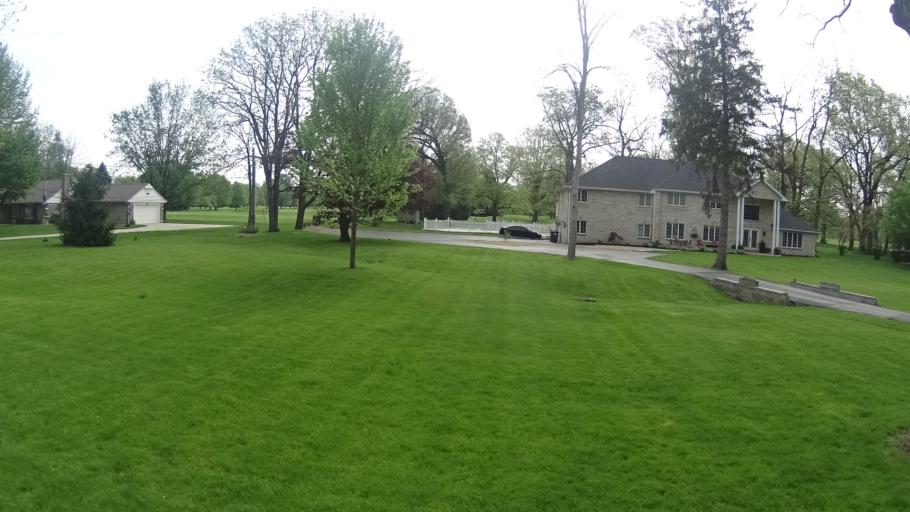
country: US
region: Indiana
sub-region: Madison County
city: Anderson
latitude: 40.1272
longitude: -85.6916
